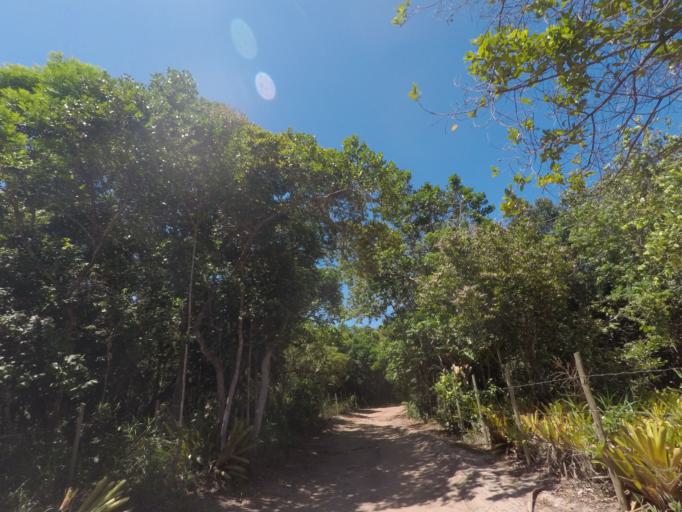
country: BR
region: Bahia
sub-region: Marau
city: Marau
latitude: -14.0140
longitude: -38.9453
